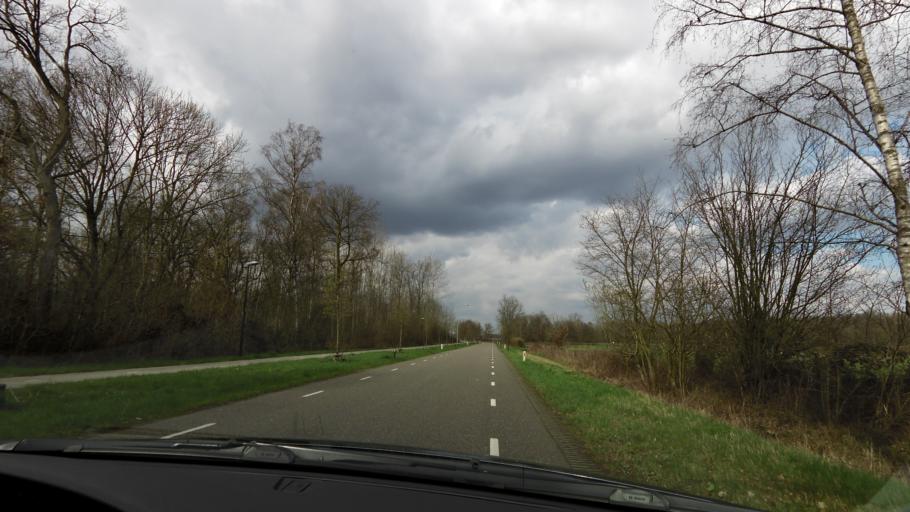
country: NL
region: Limburg
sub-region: Gemeente Sittard-Geleen
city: Limbricht
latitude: 51.0503
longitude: 5.8643
